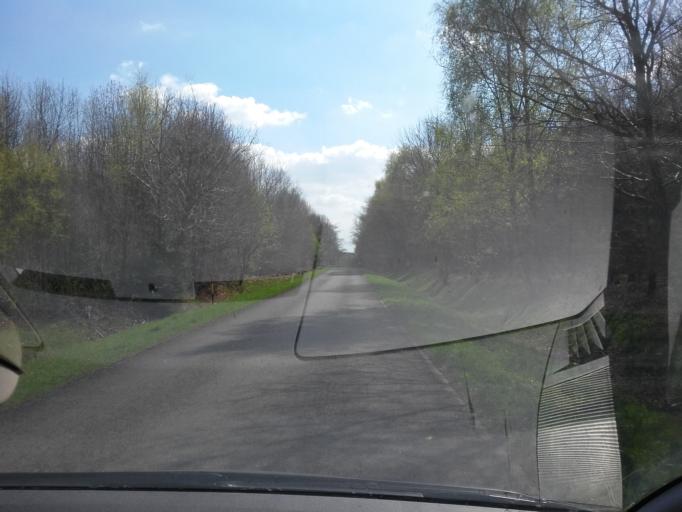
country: BE
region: Wallonia
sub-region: Province du Luxembourg
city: Habay-la-Vieille
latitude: 49.7365
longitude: 5.6587
